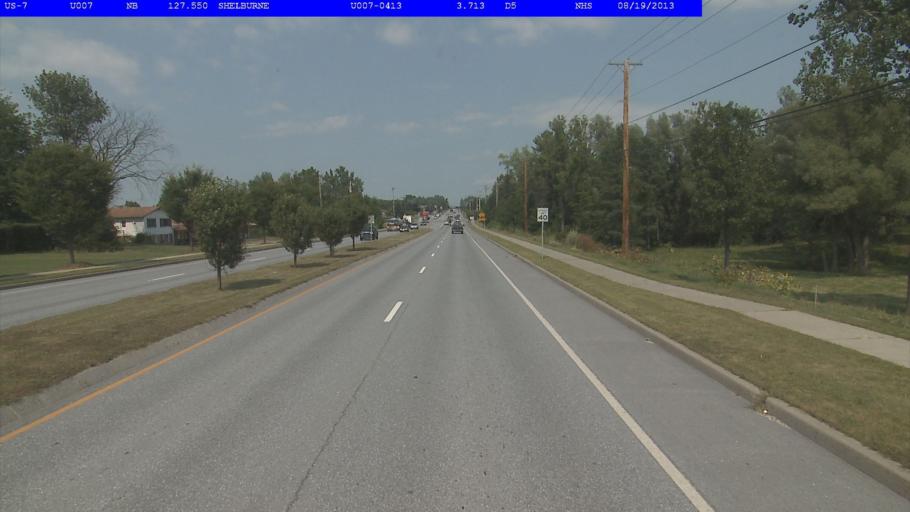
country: US
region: Vermont
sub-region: Chittenden County
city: Burlington
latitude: 44.4039
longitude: -73.2173
